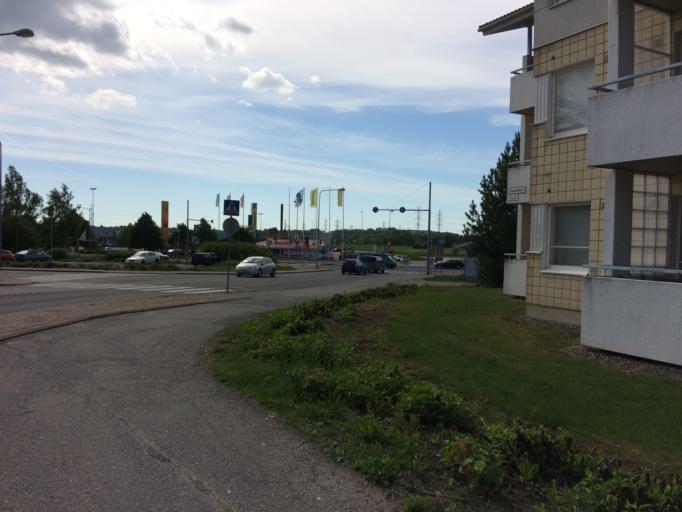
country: FI
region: Varsinais-Suomi
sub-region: Turku
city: Turku
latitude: 60.4703
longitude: 22.3097
